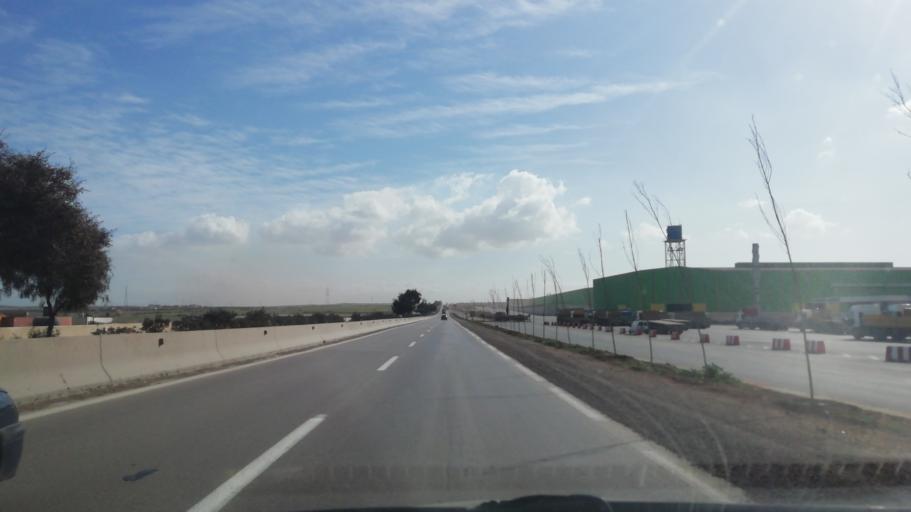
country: DZ
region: Oran
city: Ain el Bya
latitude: 35.7767
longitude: -0.2594
